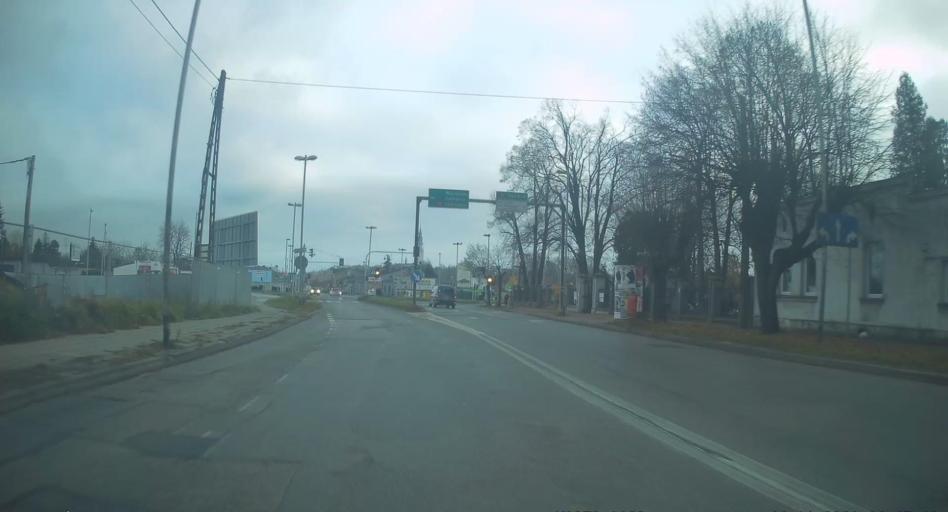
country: PL
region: Silesian Voivodeship
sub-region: Czestochowa
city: Czestochowa
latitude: 50.8195
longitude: 19.0866
